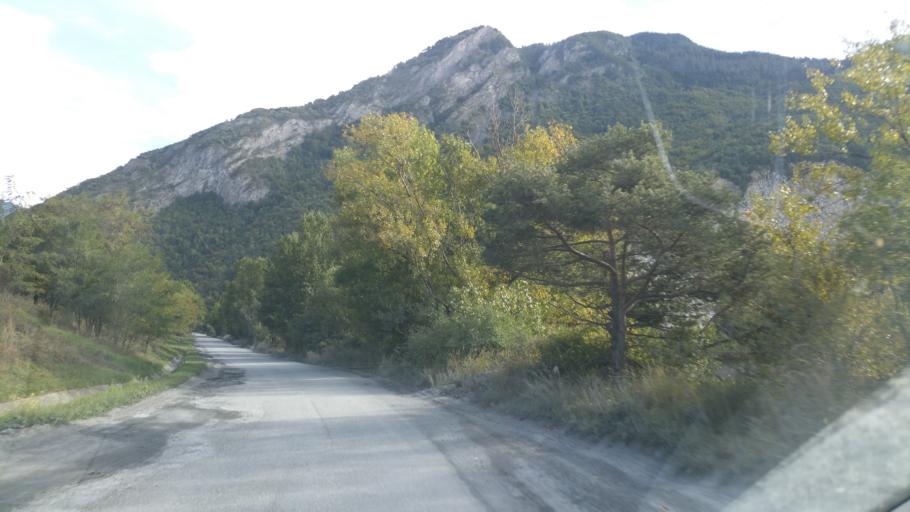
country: FR
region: Rhone-Alpes
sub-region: Departement de la Savoie
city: Saint-Michel-de-Maurienne
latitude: 45.2419
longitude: 6.4317
